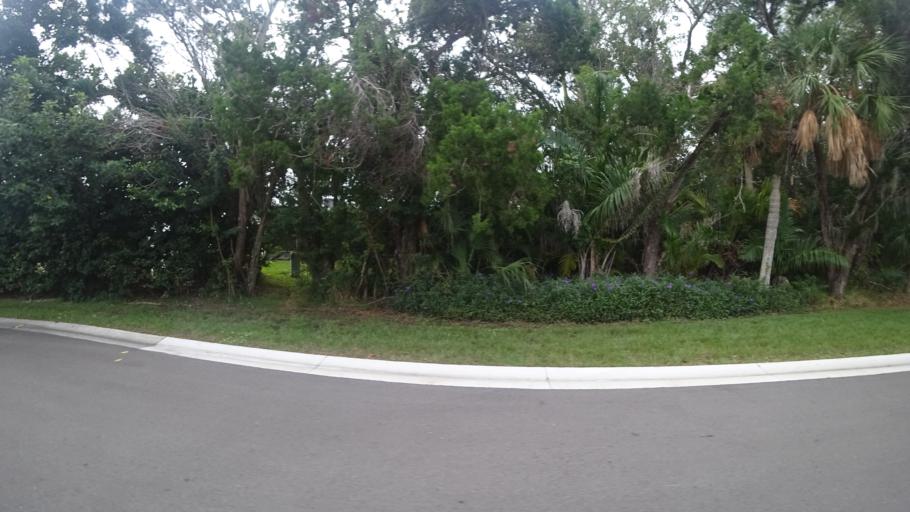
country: US
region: Florida
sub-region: Manatee County
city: Longboat Key
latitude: 27.4192
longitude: -82.6615
